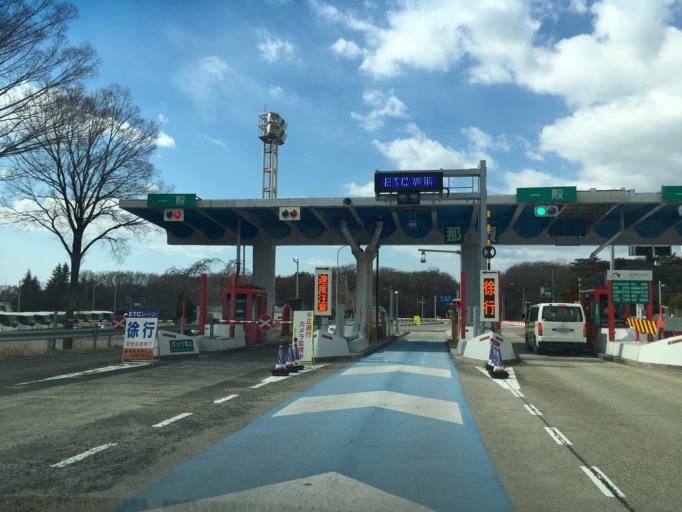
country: JP
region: Tochigi
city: Kuroiso
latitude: 37.0033
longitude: 140.0397
